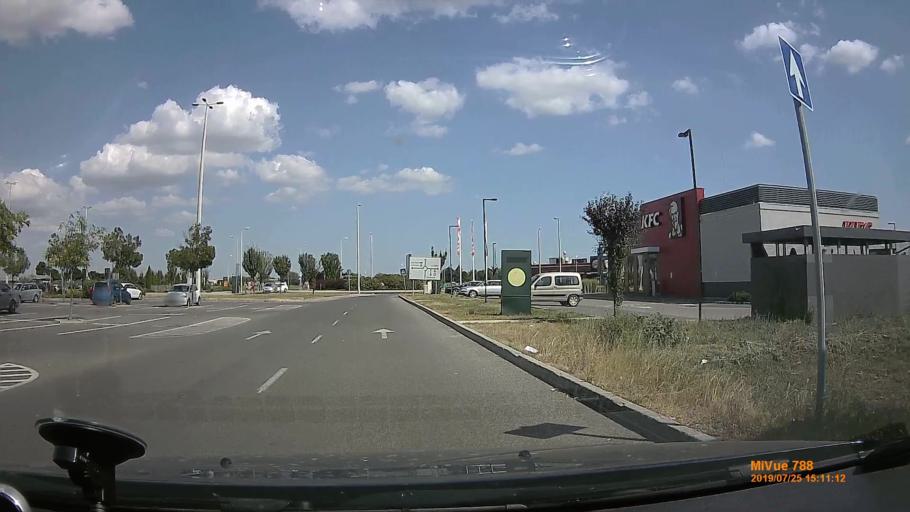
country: HU
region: Borsod-Abauj-Zemplen
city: Felsozsolca
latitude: 48.1076
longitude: 20.8361
